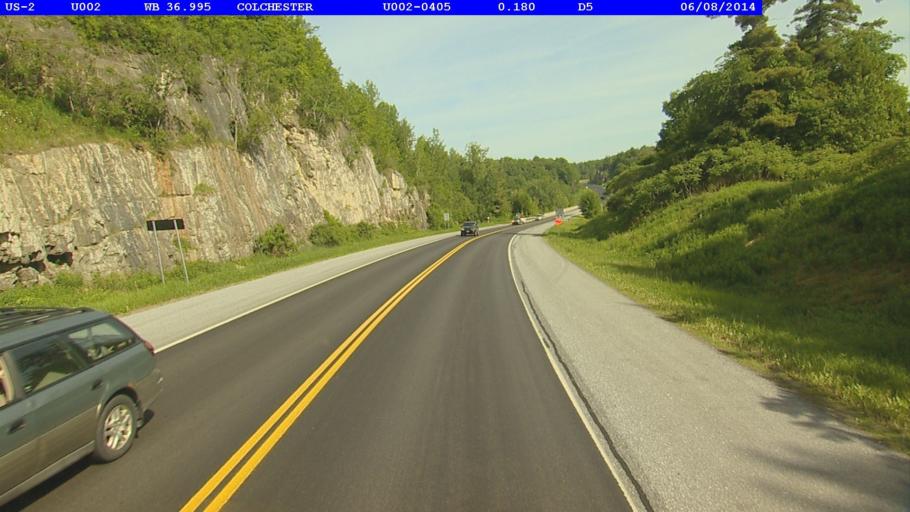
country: US
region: Vermont
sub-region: Chittenden County
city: Colchester
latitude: 44.6011
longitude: -73.2033
